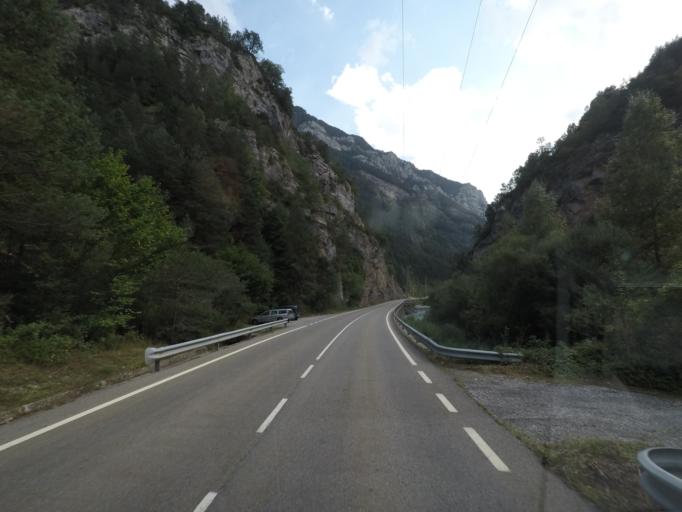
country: ES
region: Aragon
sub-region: Provincia de Huesca
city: Bielsa
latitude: 42.6034
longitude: 0.2400
